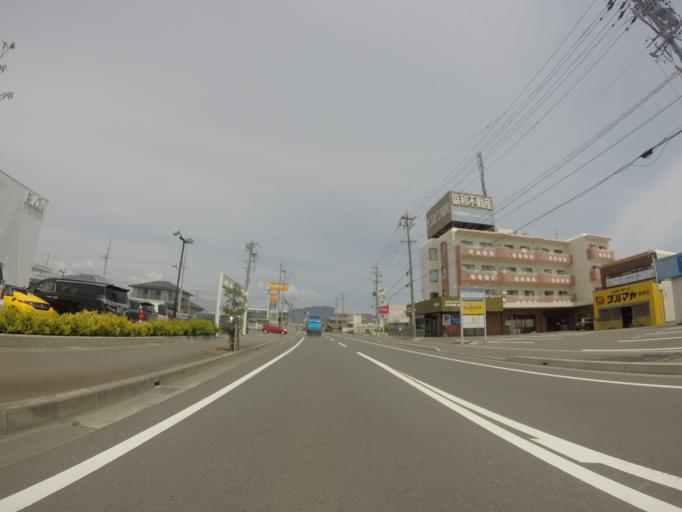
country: JP
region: Shizuoka
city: Yaizu
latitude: 34.8469
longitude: 138.3180
